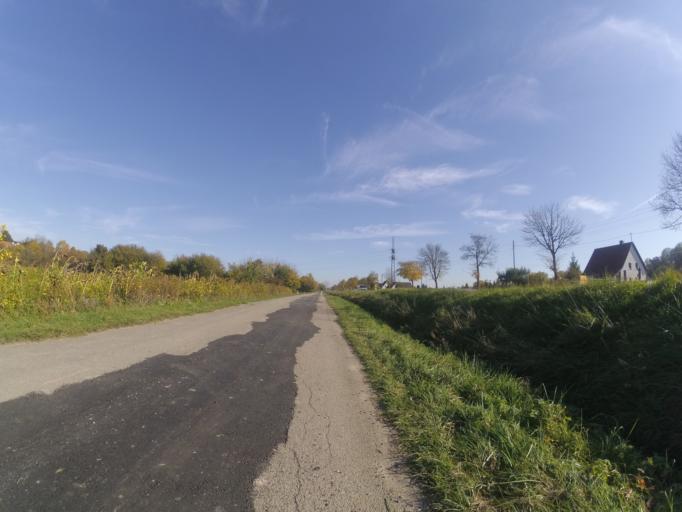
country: DE
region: Baden-Wuerttemberg
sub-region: Tuebingen Region
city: Ulm
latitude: 48.4064
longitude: 9.9348
